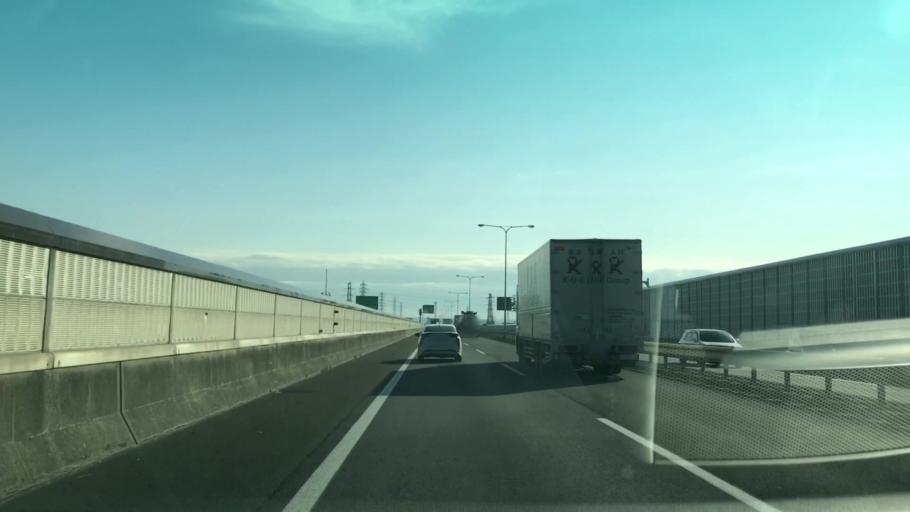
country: JP
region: Hokkaido
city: Sapporo
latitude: 43.0963
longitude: 141.3965
